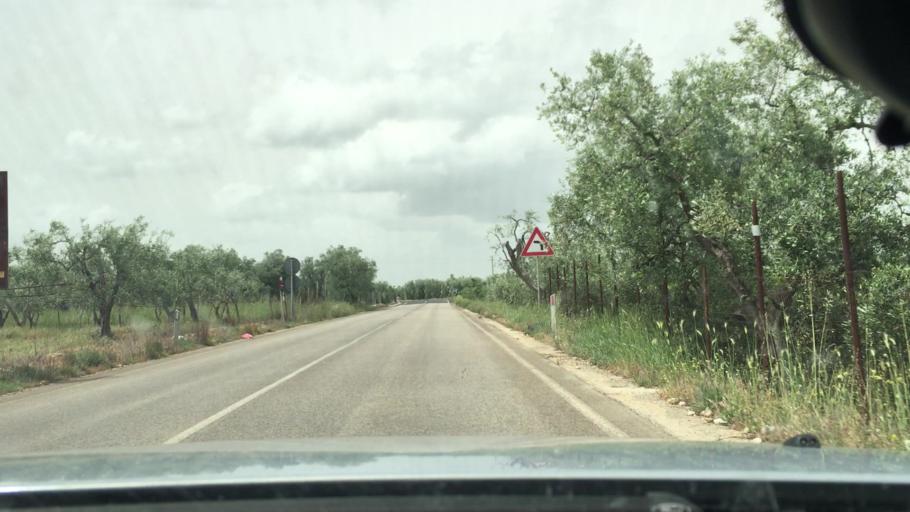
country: IT
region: Apulia
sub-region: Provincia di Bari
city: Capurso
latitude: 41.0411
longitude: 16.9478
